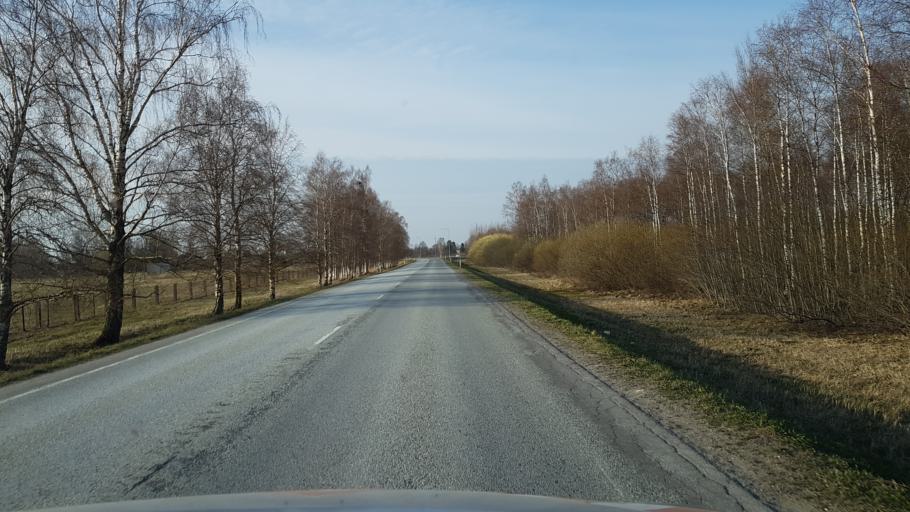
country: EE
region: Laeaene-Virumaa
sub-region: Someru vald
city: Someru
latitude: 59.3861
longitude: 26.3936
